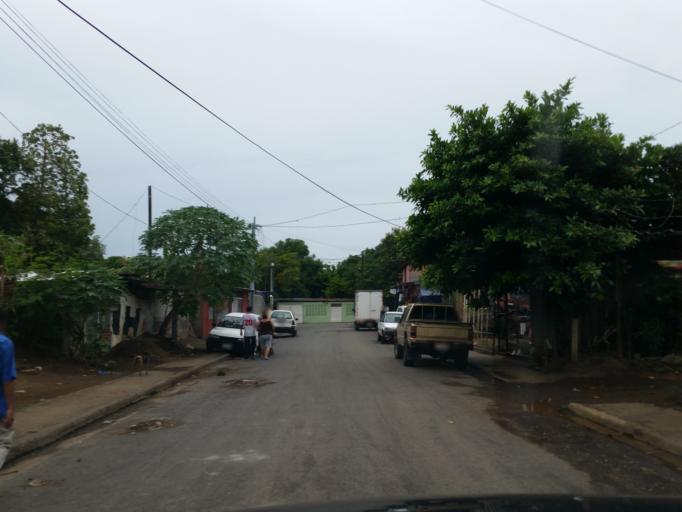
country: NI
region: Managua
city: Managua
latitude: 12.1304
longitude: -86.2762
